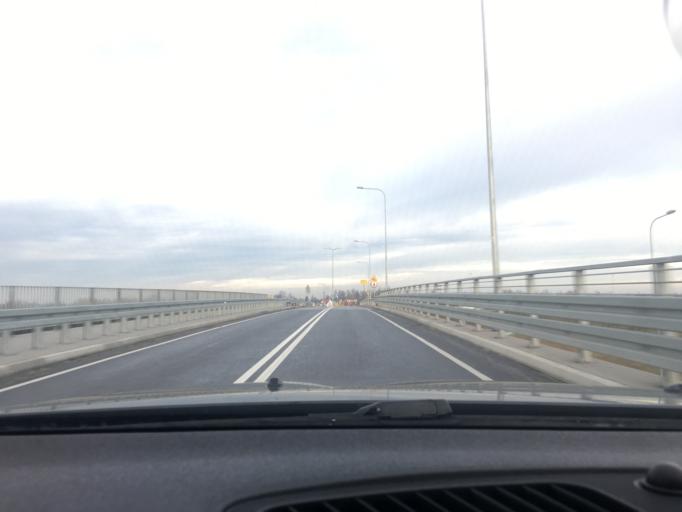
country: PL
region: Swietokrzyskie
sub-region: Powiat jedrzejowski
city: Sobkow
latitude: 50.6899
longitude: 20.3702
